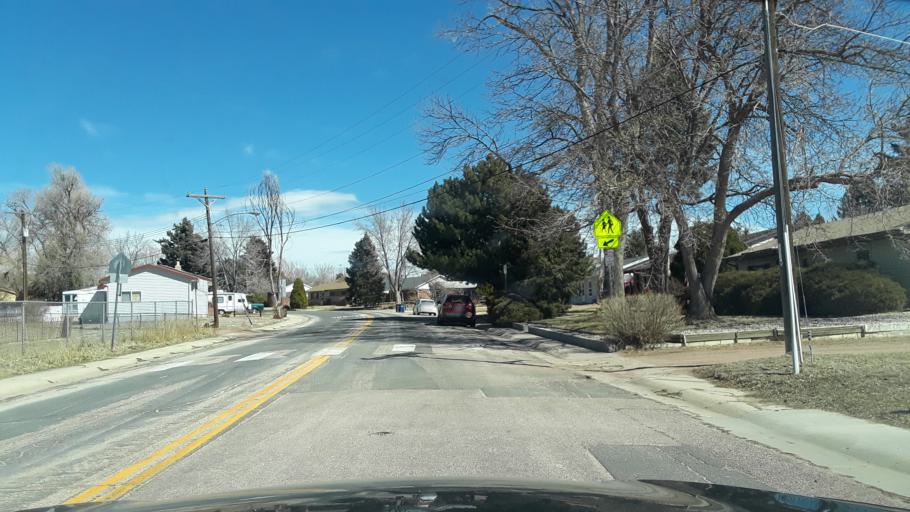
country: US
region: Colorado
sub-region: El Paso County
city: Colorado Springs
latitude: 38.8769
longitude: -104.8015
